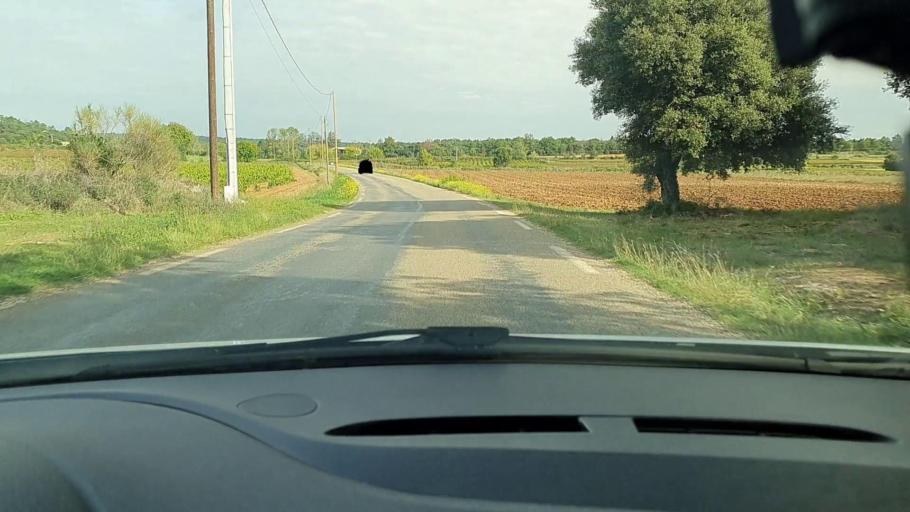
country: FR
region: Languedoc-Roussillon
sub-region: Departement du Gard
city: Saint-Quentin-la-Poterie
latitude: 44.0920
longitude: 4.4555
